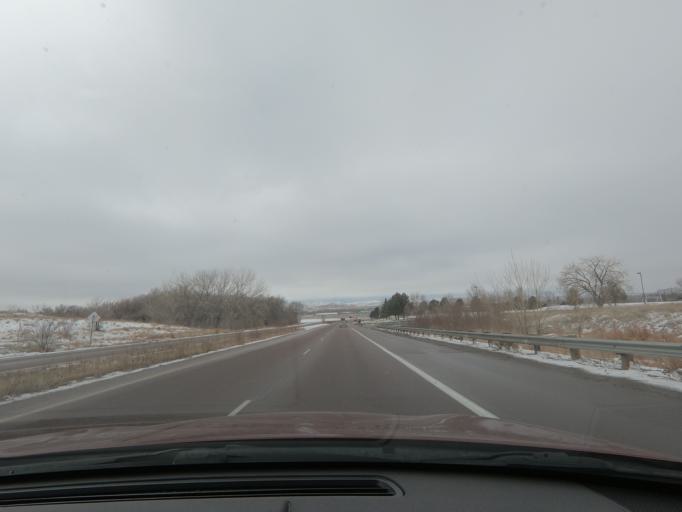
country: US
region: Colorado
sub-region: El Paso County
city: Security-Widefield
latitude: 38.7201
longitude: -104.7053
